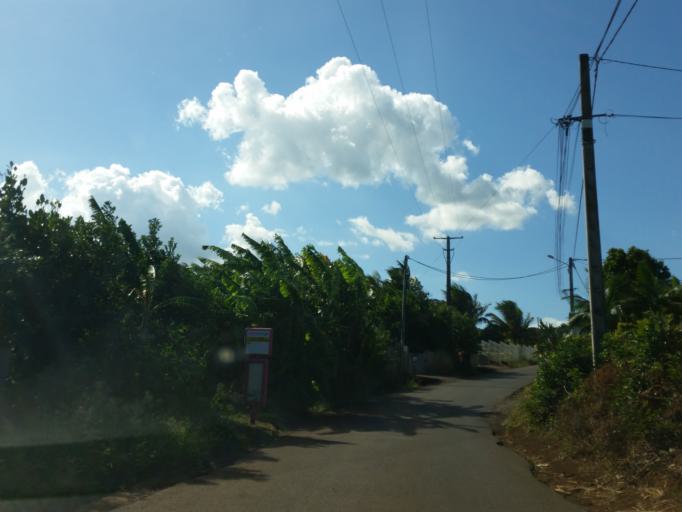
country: RE
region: Reunion
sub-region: Reunion
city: Saint-Pierre
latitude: -21.3205
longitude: 55.5022
